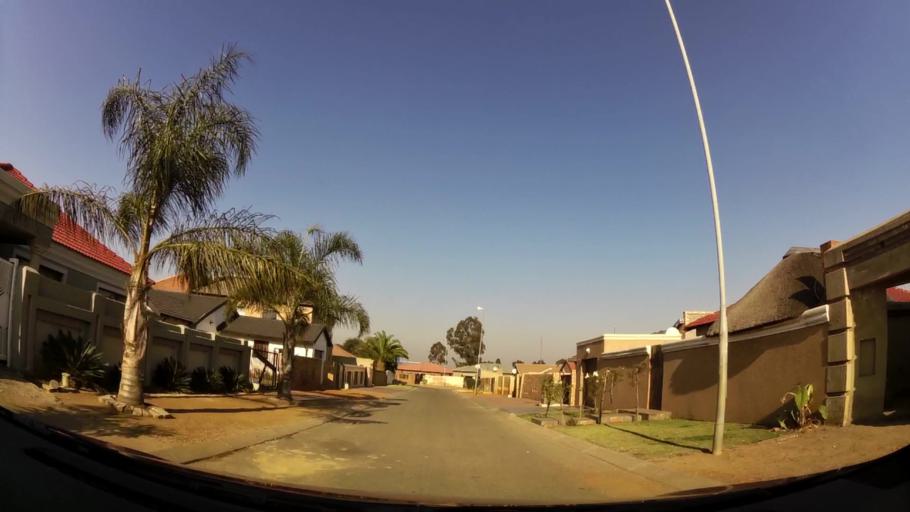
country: ZA
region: Gauteng
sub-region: City of Johannesburg Metropolitan Municipality
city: Soweto
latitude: -26.2929
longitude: 27.9478
